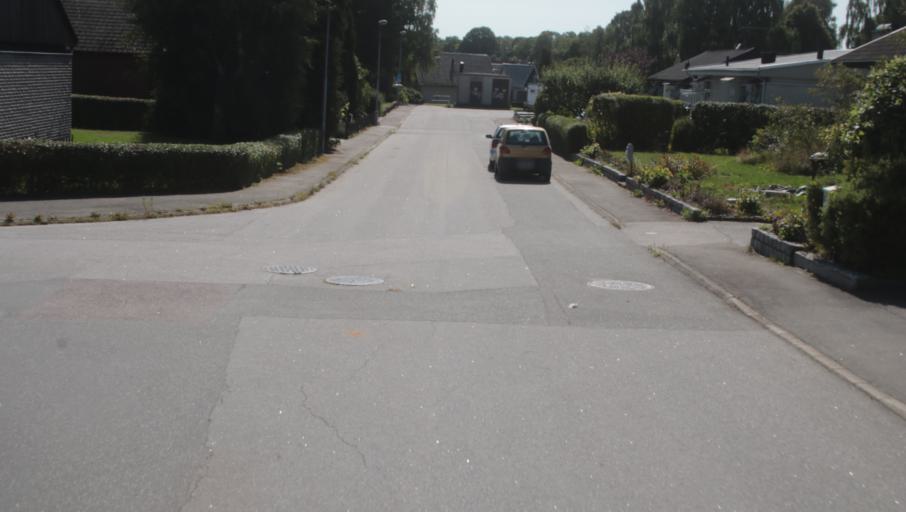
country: SE
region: Blekinge
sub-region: Karlshamns Kommun
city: Karlshamn
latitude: 56.2114
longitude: 14.8436
